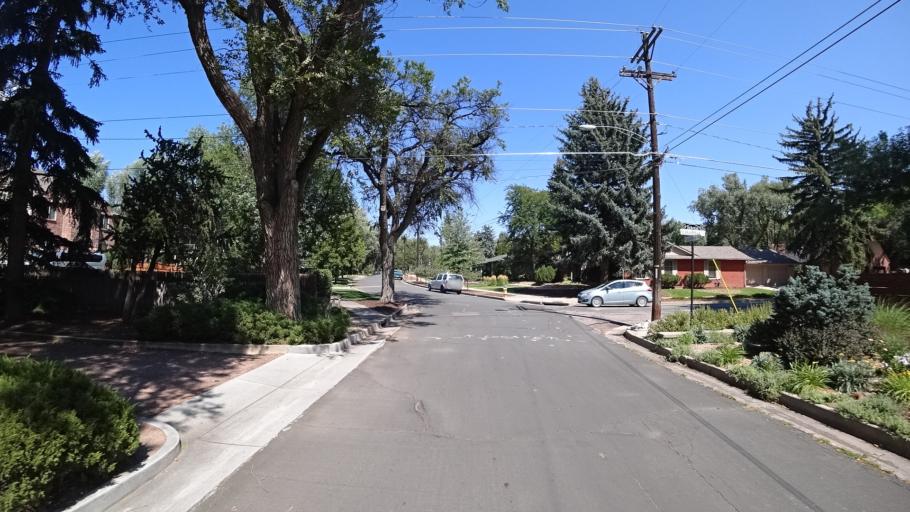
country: US
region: Colorado
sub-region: El Paso County
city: Colorado Springs
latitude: 38.8539
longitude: -104.8286
